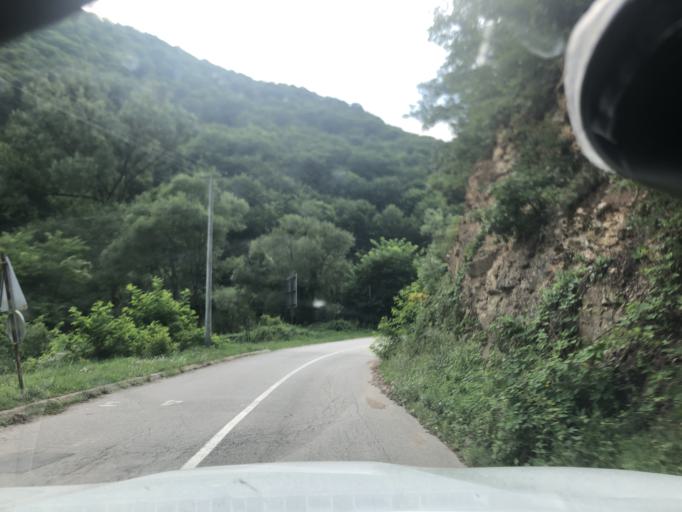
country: RS
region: Central Serbia
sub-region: Jablanicki Okrug
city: Medvega
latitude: 42.7797
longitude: 21.5983
